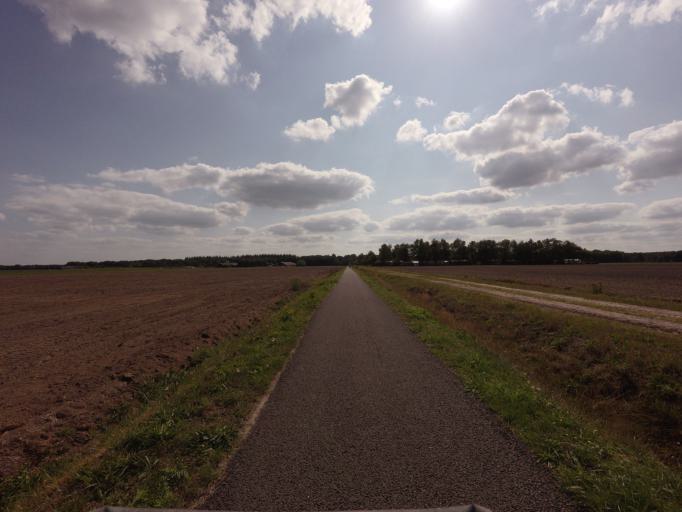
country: NL
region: Drenthe
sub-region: Gemeente Westerveld
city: Dwingeloo
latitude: 52.8443
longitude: 6.4674
